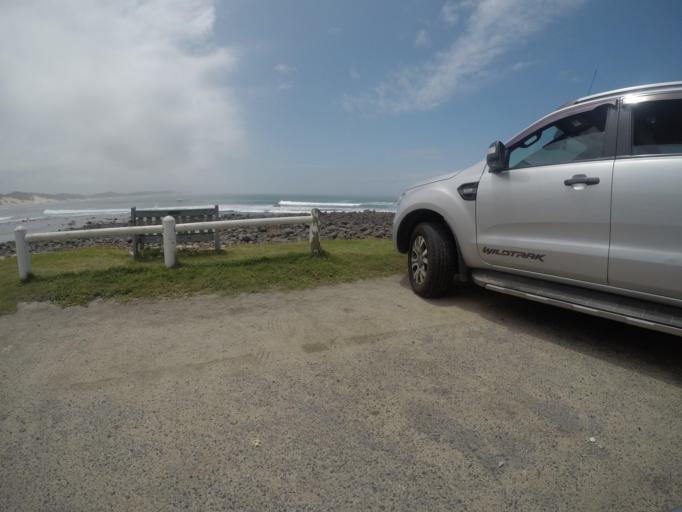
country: ZA
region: Eastern Cape
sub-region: Buffalo City Metropolitan Municipality
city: East London
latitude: -32.9957
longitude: 27.9509
